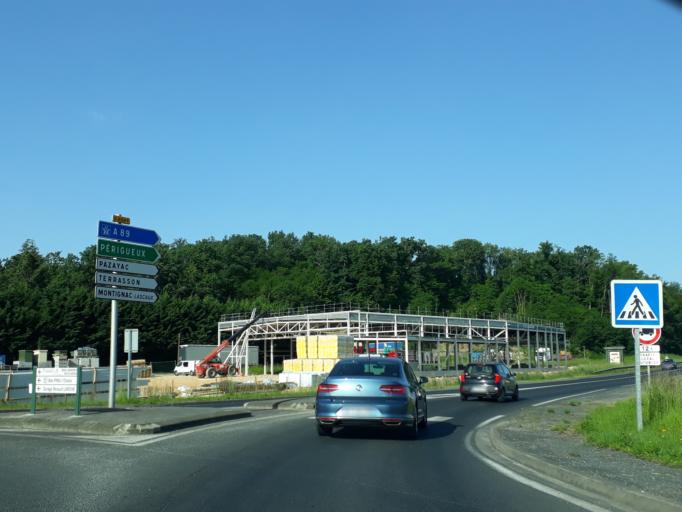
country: FR
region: Limousin
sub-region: Departement de la Correze
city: Larche
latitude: 45.1248
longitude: 1.4079
